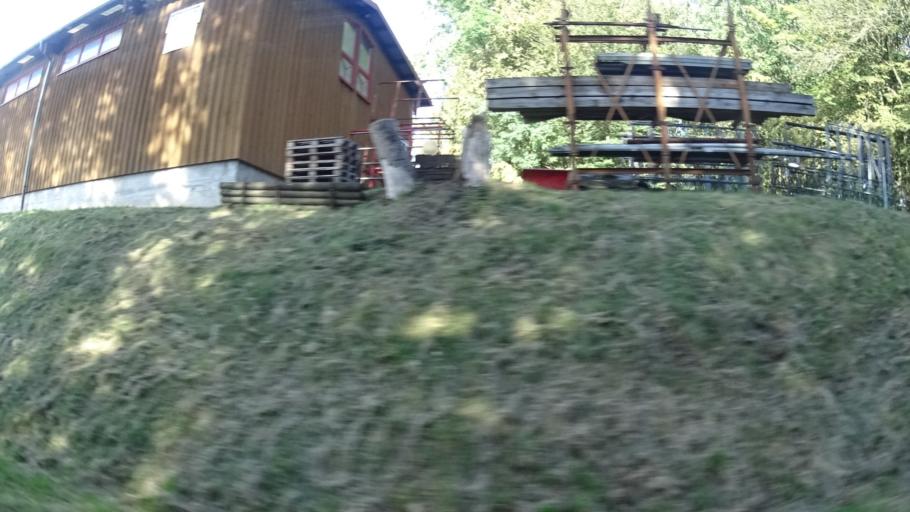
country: DE
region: Hesse
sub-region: Regierungsbezirk Kassel
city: Poppenhausen
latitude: 50.5373
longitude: 9.8653
